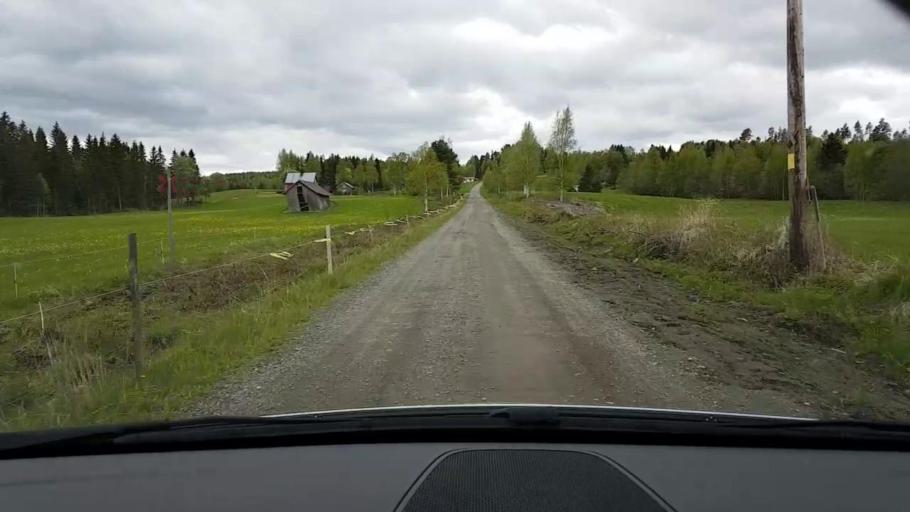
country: SE
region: Jaemtland
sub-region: Bergs Kommun
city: Hoverberg
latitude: 62.8261
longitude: 14.4091
